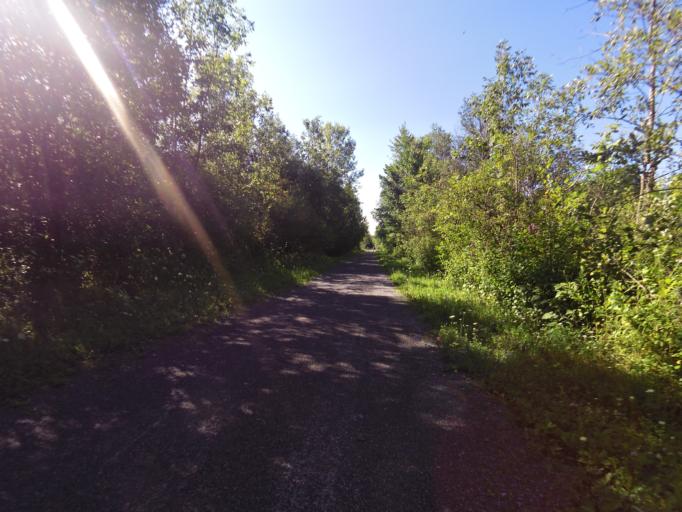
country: CA
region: Ontario
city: Ottawa
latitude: 45.2372
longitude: -75.6194
